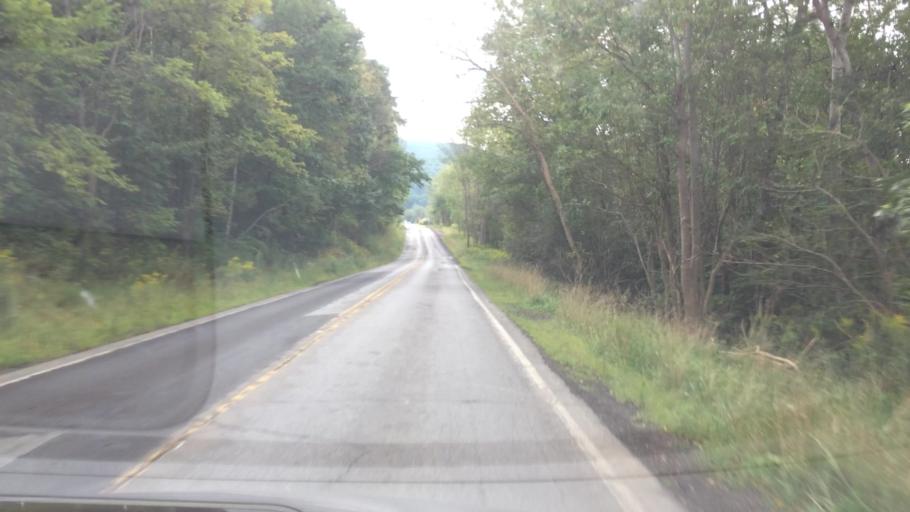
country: US
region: Pennsylvania
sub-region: McKean County
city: Bradford
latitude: 41.9189
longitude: -78.6439
